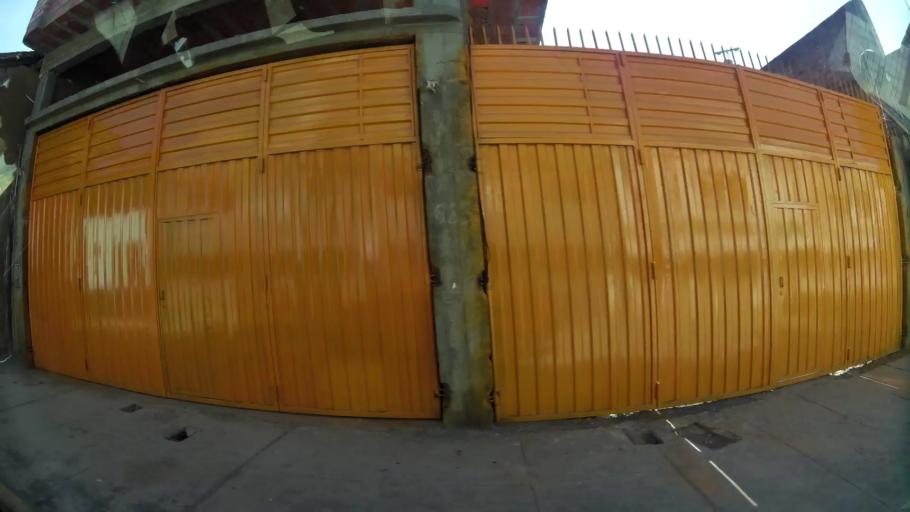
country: PE
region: Junin
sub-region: Provincia de Huancayo
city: San Jeronimo
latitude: -11.9477
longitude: -75.2846
